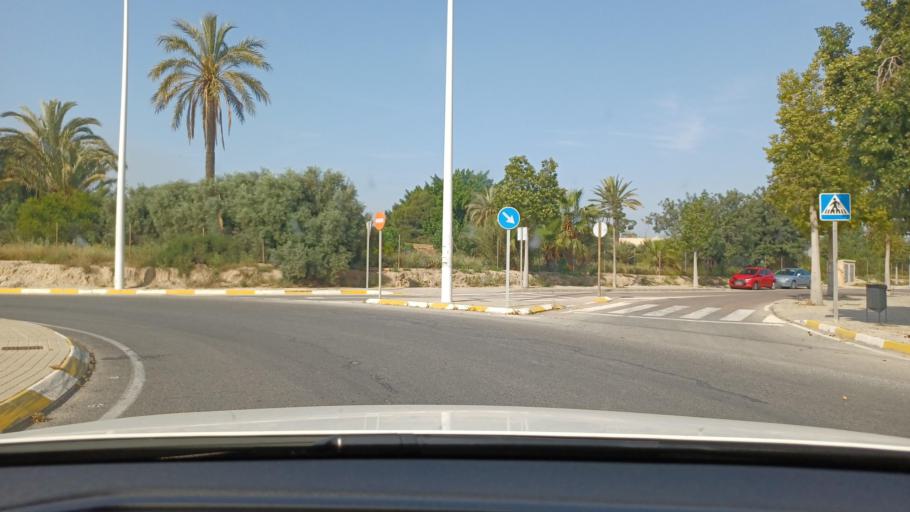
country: ES
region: Valencia
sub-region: Provincia de Alicante
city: Elche
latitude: 38.2450
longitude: -0.7066
